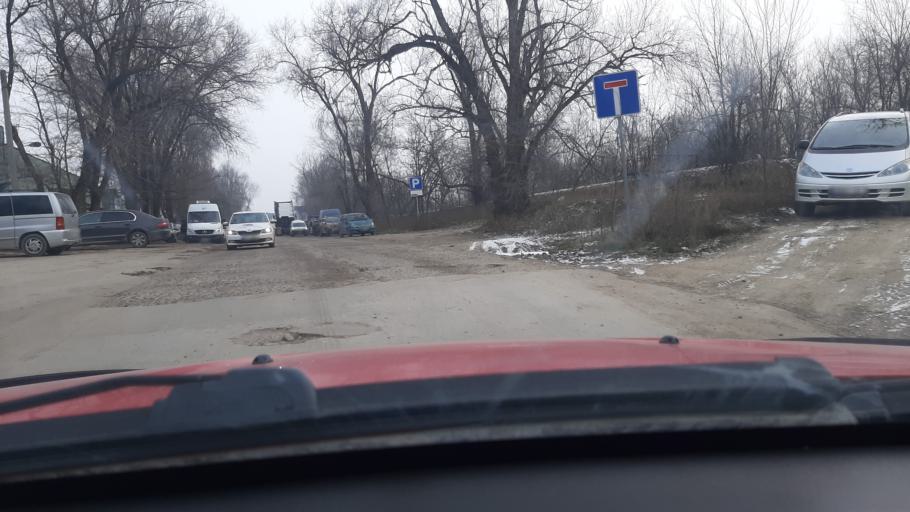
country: MD
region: Chisinau
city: Chisinau
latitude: 46.9743
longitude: 28.8954
